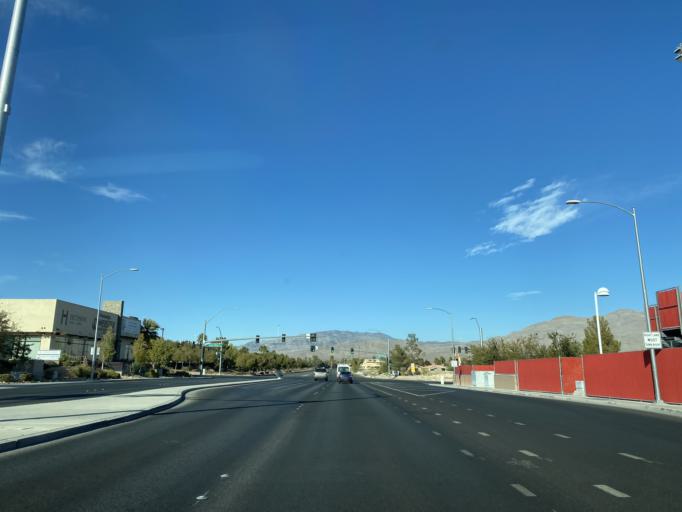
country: US
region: Nevada
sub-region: Clark County
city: North Las Vegas
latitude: 36.3041
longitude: -115.2601
